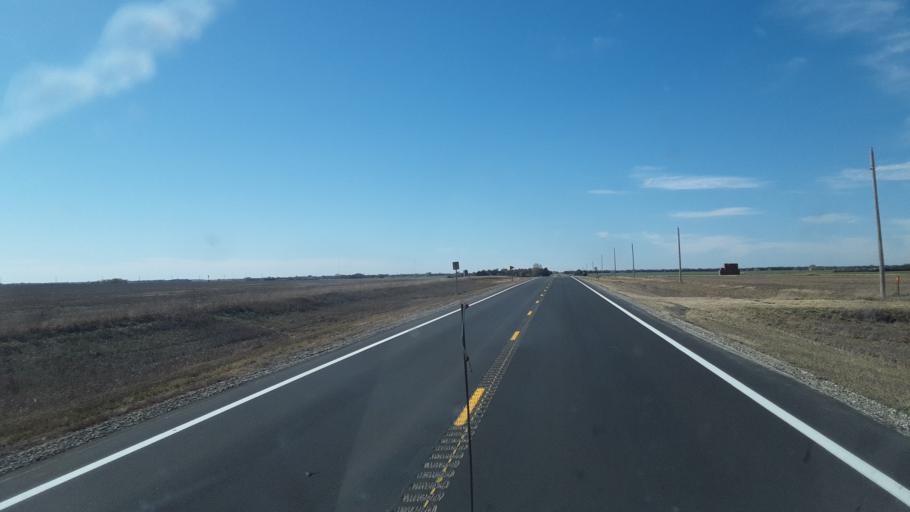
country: US
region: Kansas
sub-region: Rice County
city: Lyons
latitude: 38.3765
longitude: -98.0868
